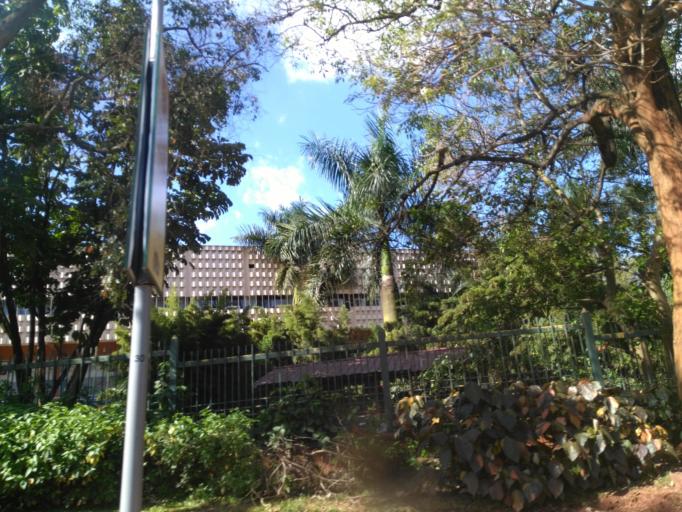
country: UG
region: Central Region
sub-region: Kampala District
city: Kampala
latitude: 0.3170
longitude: 32.5866
